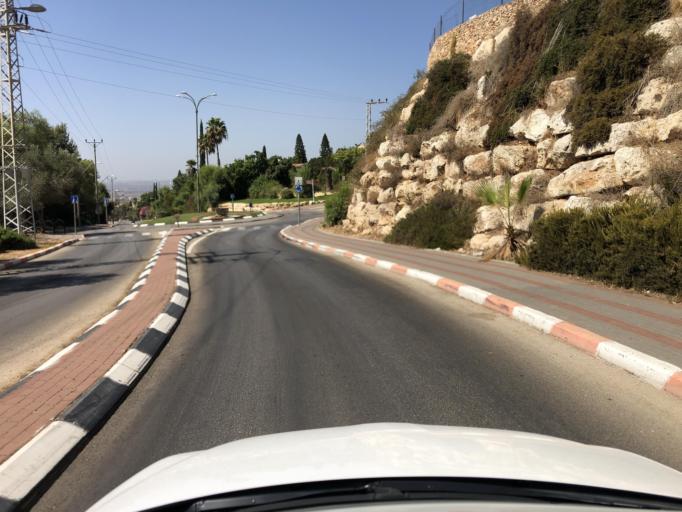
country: PS
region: West Bank
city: An Nabi Ilyas
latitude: 32.1745
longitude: 35.0111
